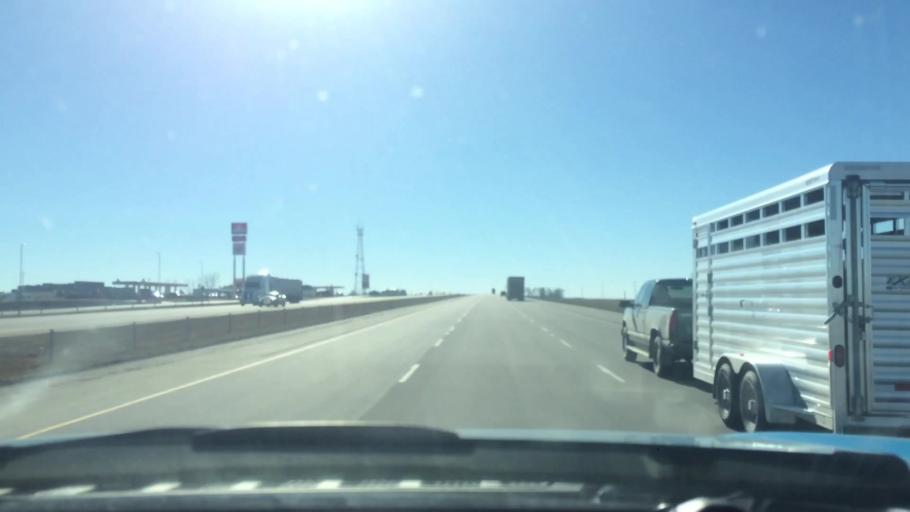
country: CA
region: Alberta
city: Crossfield
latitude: 51.4163
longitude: -114.0020
